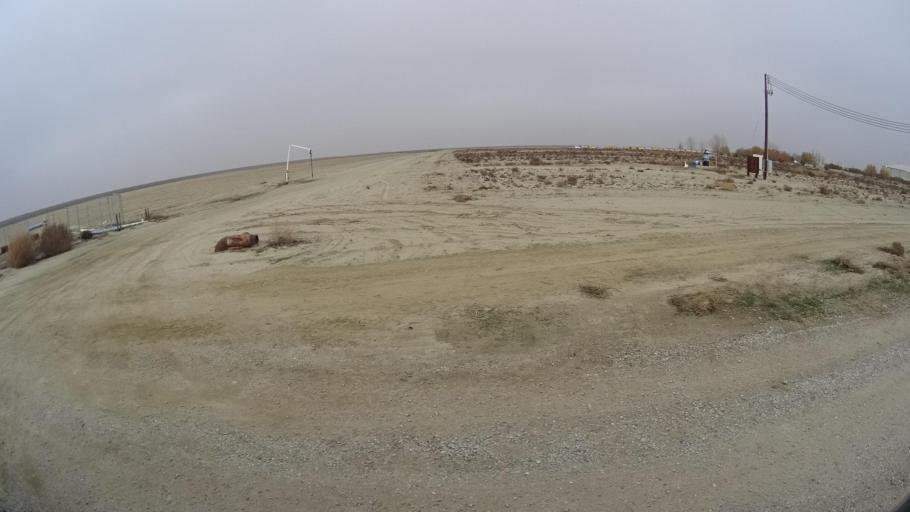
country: US
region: California
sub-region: Kern County
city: Maricopa
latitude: 35.0940
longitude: -119.2028
